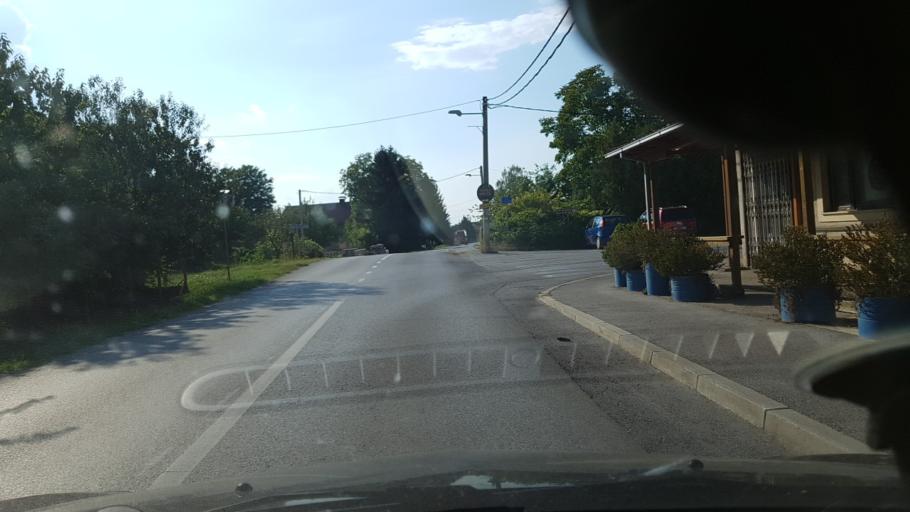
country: HR
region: Zagrebacka
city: Bregana
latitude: 45.8887
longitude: 15.6925
